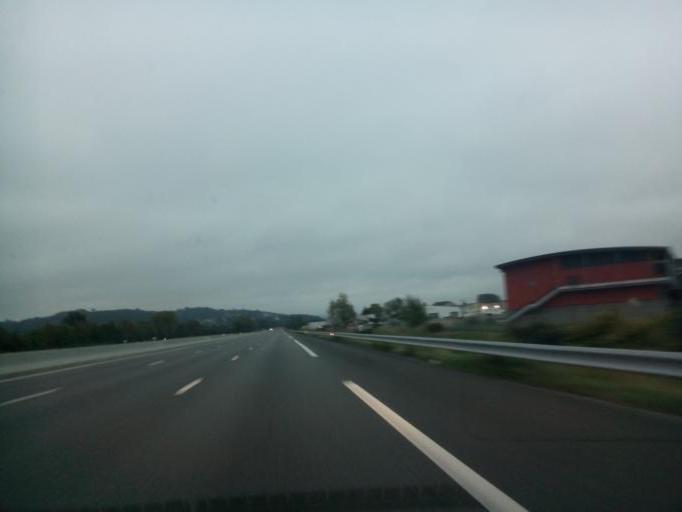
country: FR
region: Rhone-Alpes
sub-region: Departement de l'Isere
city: Domarin
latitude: 45.6042
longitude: 5.2515
